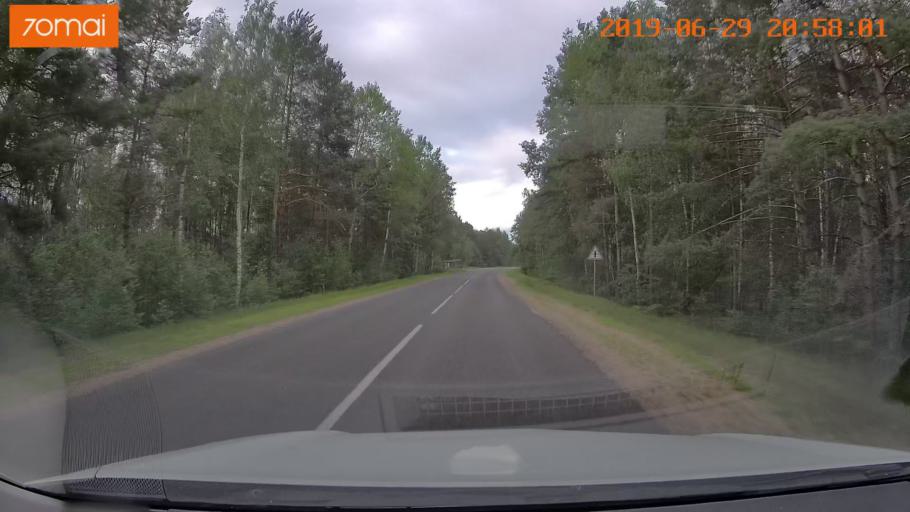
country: BY
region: Brest
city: Hantsavichy
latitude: 52.7260
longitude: 26.3782
